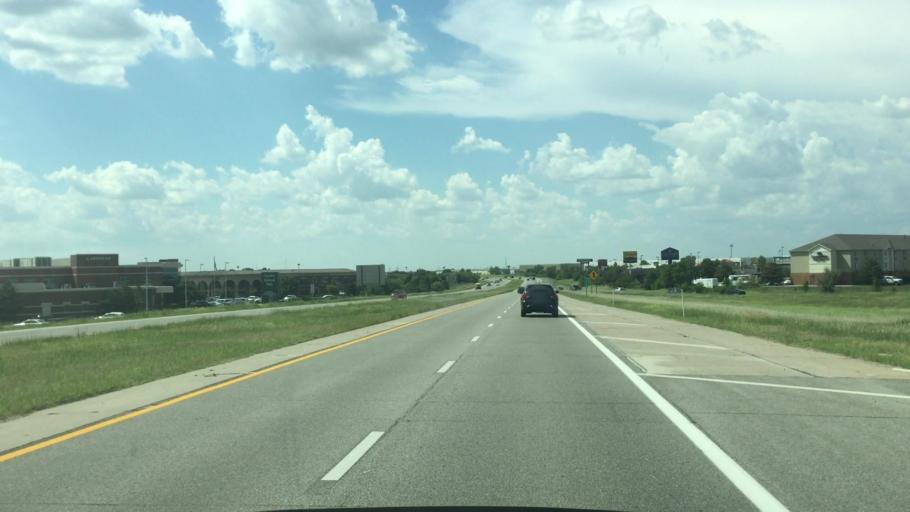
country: US
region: Kansas
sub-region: Sedgwick County
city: Bellaire
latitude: 37.7389
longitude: -97.2276
